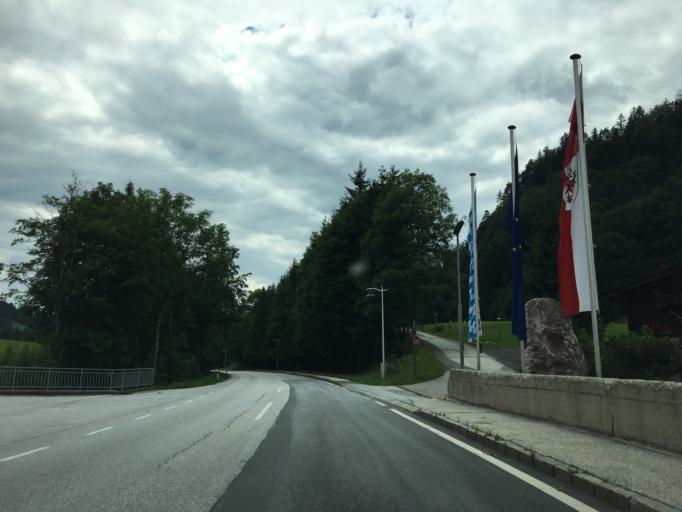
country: AT
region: Tyrol
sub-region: Politischer Bezirk Kufstein
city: Rettenschoss
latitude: 47.6397
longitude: 12.2817
